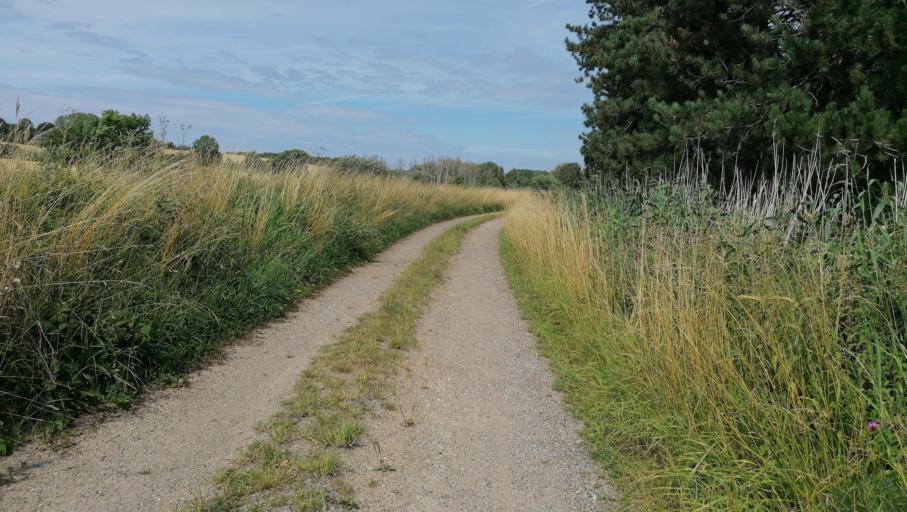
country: DK
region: Zealand
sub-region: Odsherred Kommune
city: Horve
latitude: 55.7816
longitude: 11.4189
